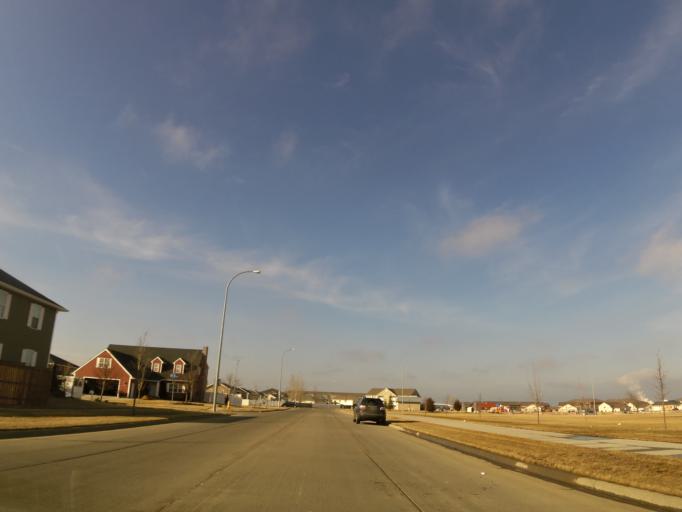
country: US
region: North Dakota
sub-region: Grand Forks County
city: Grand Forks
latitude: 47.8809
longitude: -97.0576
